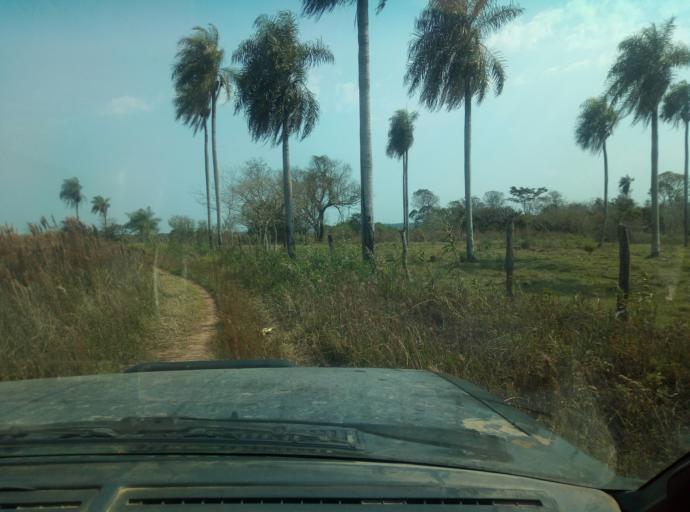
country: PY
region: Caaguazu
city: Doctor Cecilio Baez
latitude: -25.1360
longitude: -56.2417
